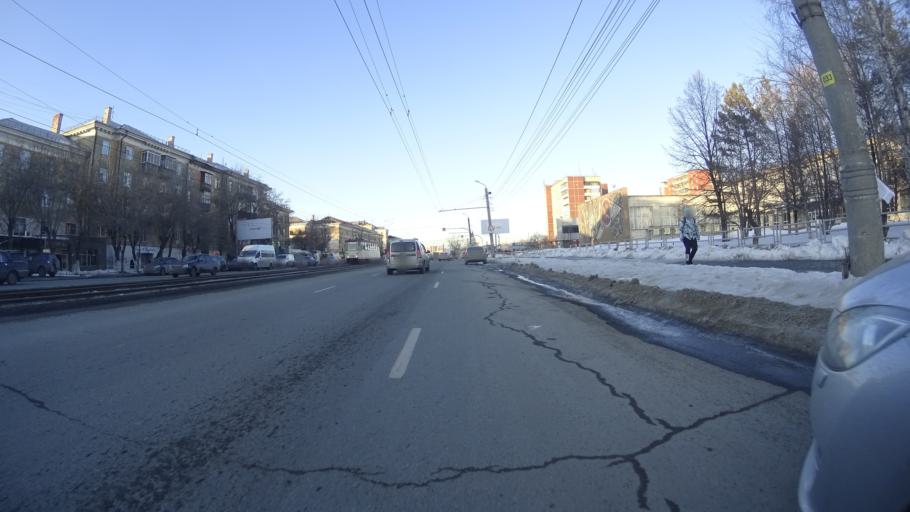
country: RU
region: Chelyabinsk
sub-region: Gorod Chelyabinsk
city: Chelyabinsk
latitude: 55.1430
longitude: 61.4435
